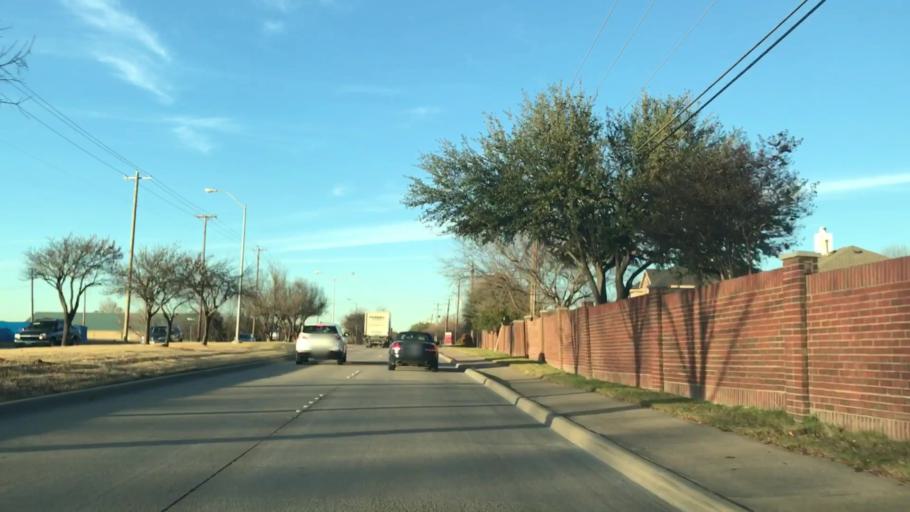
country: US
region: Texas
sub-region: Dallas County
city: Rowlett
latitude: 32.8987
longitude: -96.5181
